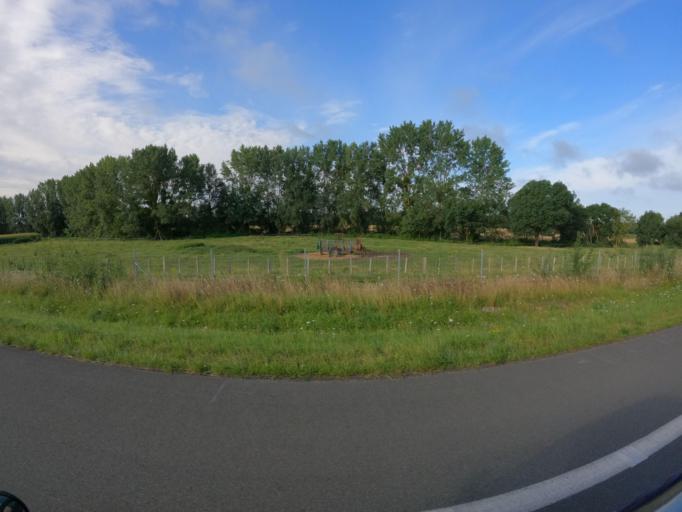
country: FR
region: Pays de la Loire
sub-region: Departement de Maine-et-Loire
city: Villebernier
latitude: 47.2945
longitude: -0.0220
